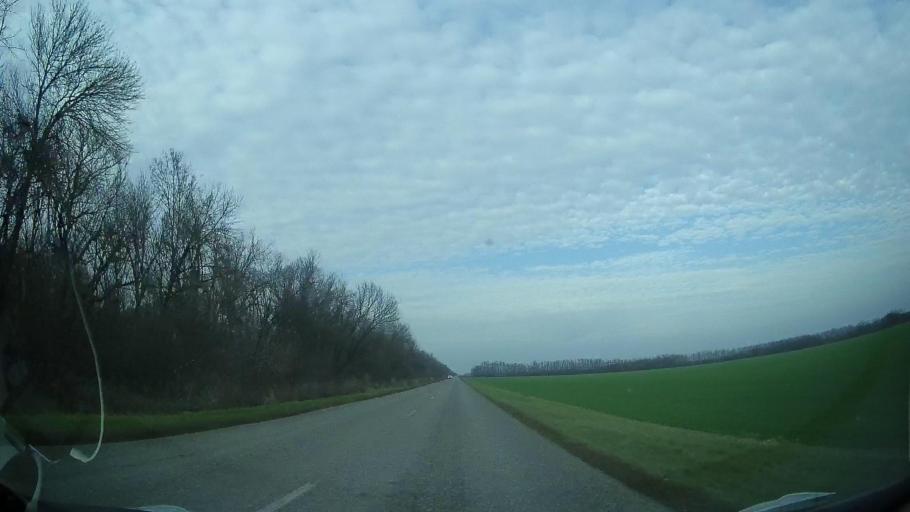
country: RU
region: Rostov
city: Zernograd
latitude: 46.9821
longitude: 40.3916
